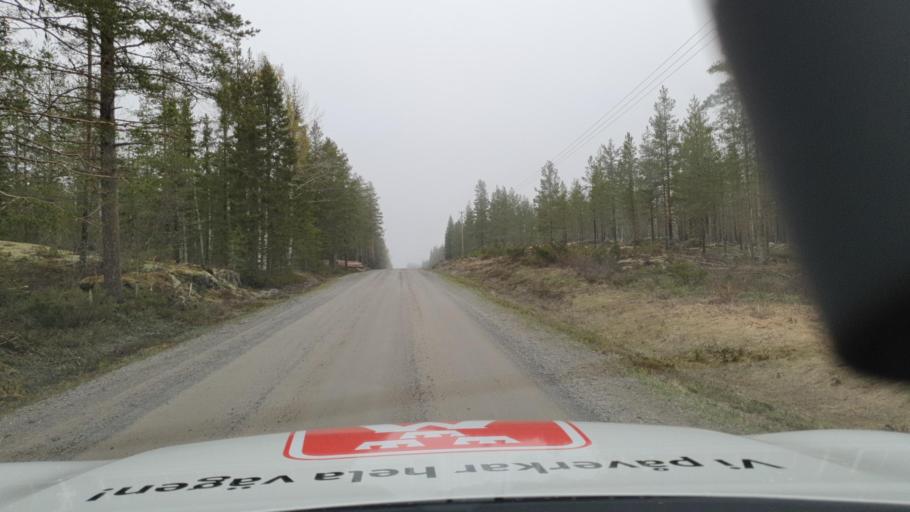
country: SE
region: Vaesterbotten
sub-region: Nordmalings Kommun
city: Nordmaling
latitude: 63.7434
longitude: 19.5017
